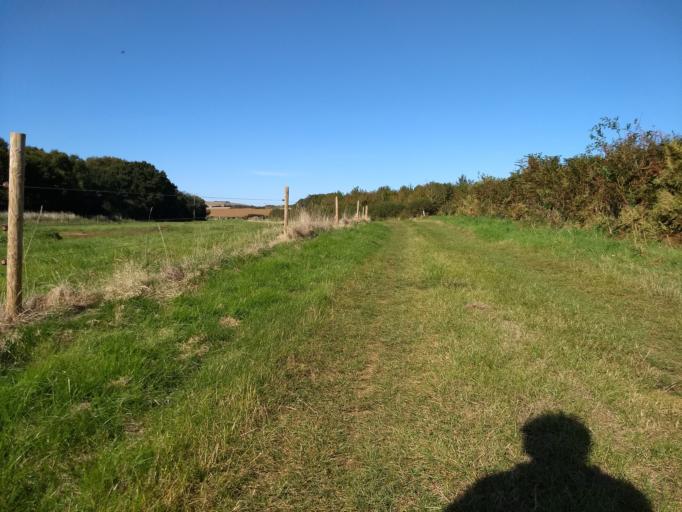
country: GB
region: England
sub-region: Isle of Wight
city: Niton
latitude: 50.6365
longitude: -1.2841
